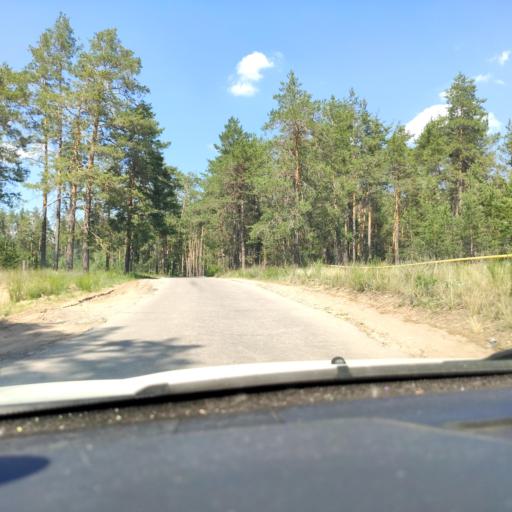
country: RU
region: Samara
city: Pribrezhnyy
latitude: 53.4794
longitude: 49.8250
